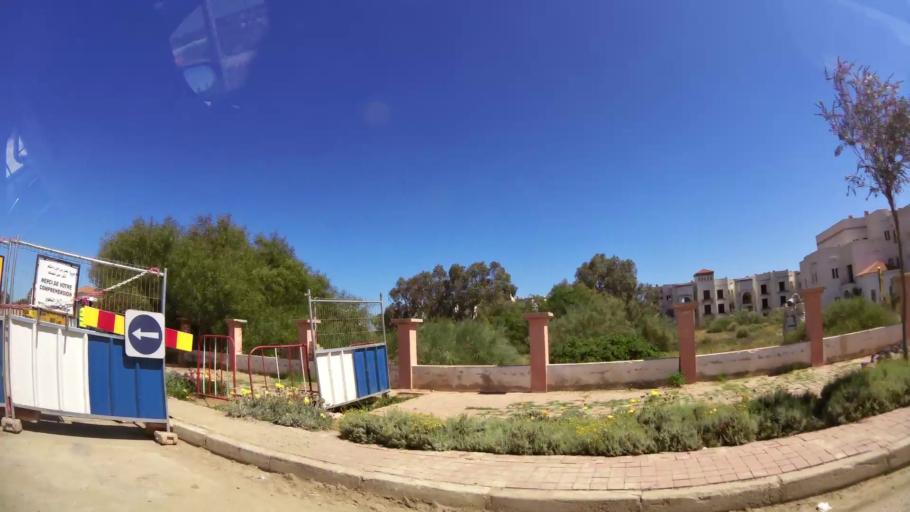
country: MA
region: Oriental
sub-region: Berkane-Taourirt
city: Madagh
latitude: 35.1101
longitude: -2.3155
